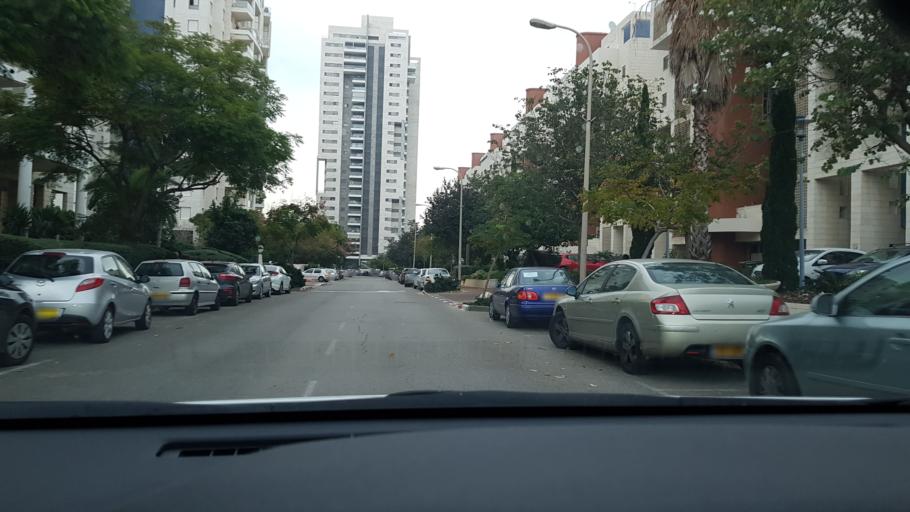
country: IL
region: Central District
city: Ness Ziona
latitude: 31.9059
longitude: 34.8209
